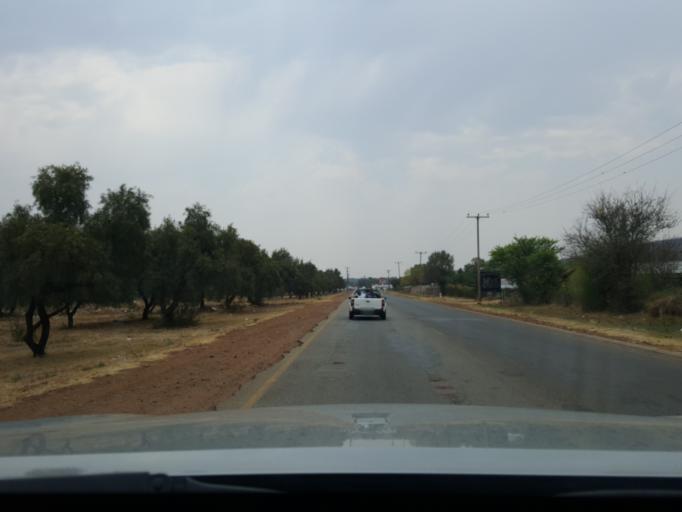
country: ZA
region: North-West
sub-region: Ngaka Modiri Molema District Municipality
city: Zeerust
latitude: -25.4981
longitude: 25.9841
